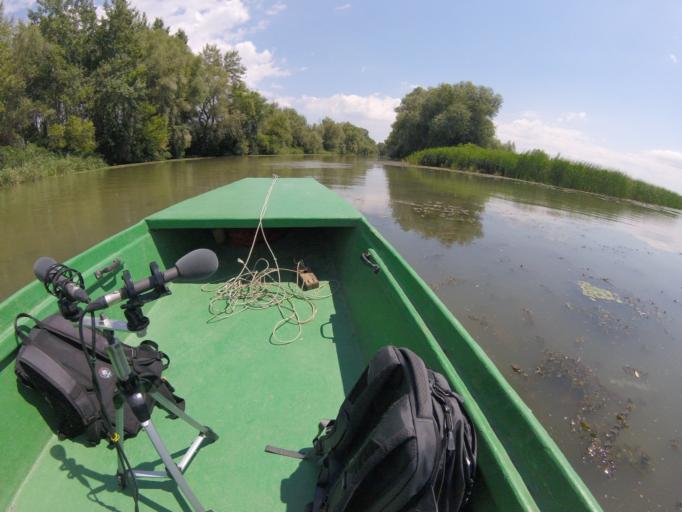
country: HU
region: Heves
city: Poroszlo
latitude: 47.5962
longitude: 20.6779
